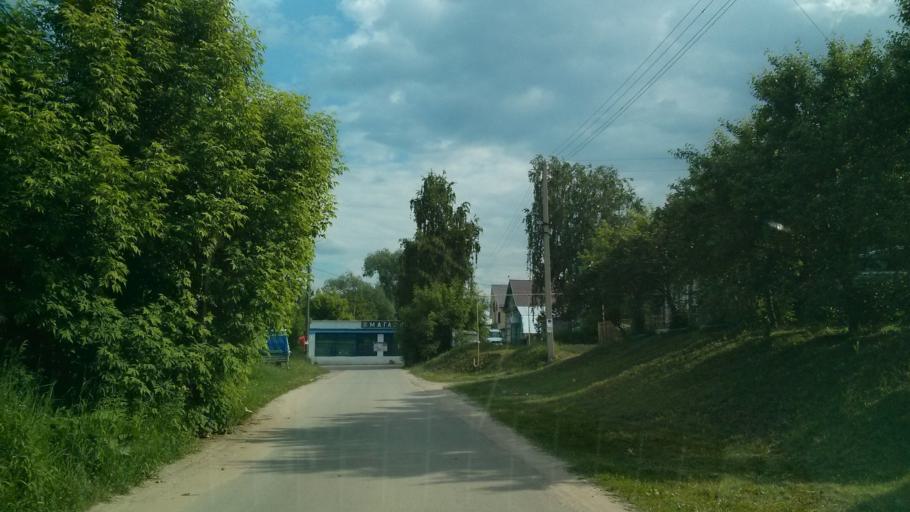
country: RU
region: Nizjnij Novgorod
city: Afonino
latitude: 56.2761
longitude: 44.1038
